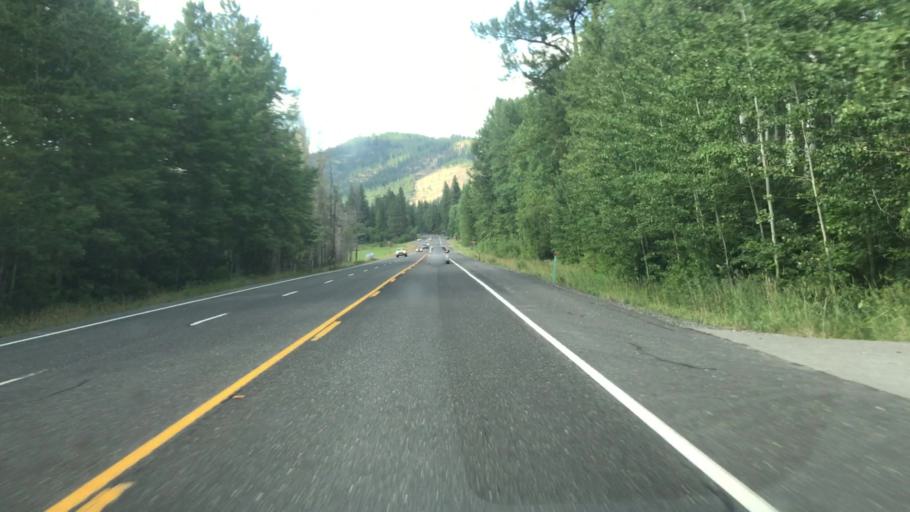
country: US
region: Washington
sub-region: Chelan County
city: Leavenworth
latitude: 47.7458
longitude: -120.7376
